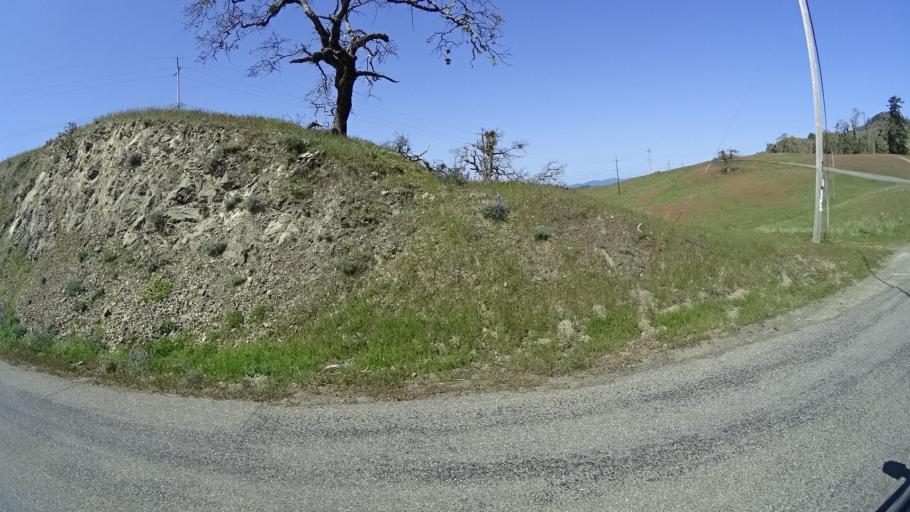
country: US
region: California
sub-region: Humboldt County
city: Redway
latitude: 40.0977
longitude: -123.6834
